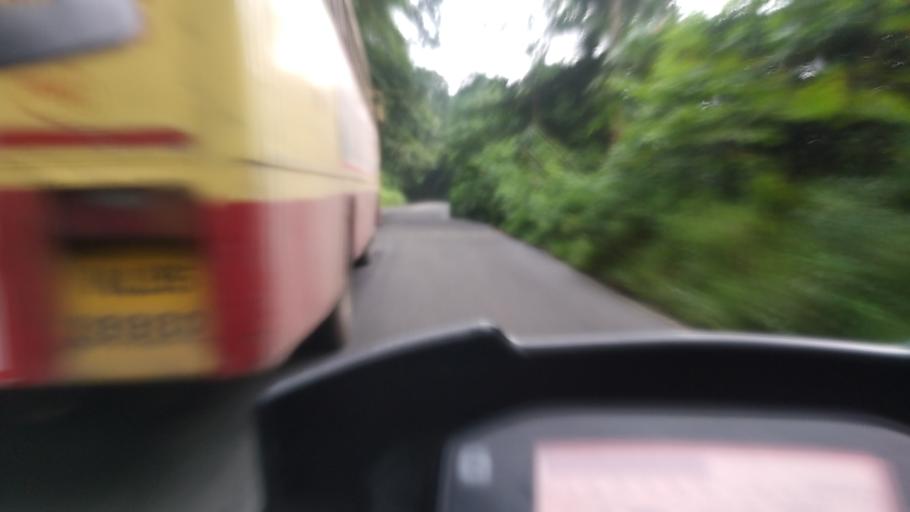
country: IN
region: Kerala
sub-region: Idukki
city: Kuttampuzha
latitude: 10.0666
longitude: 76.7822
